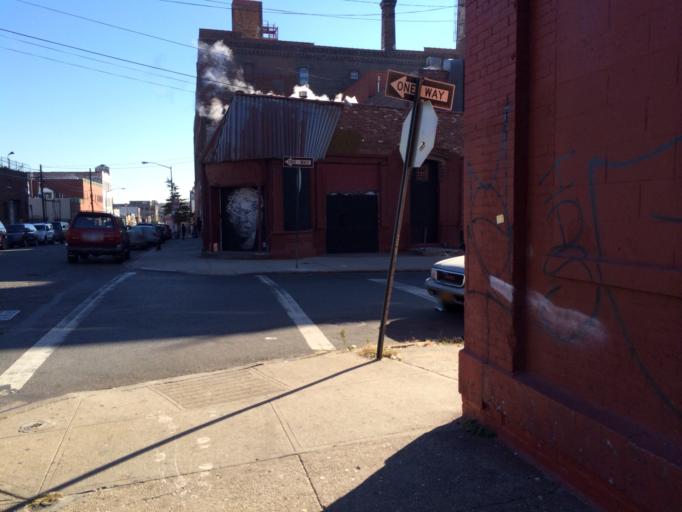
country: US
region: New York
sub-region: Queens County
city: Long Island City
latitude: 40.7085
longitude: -73.9391
